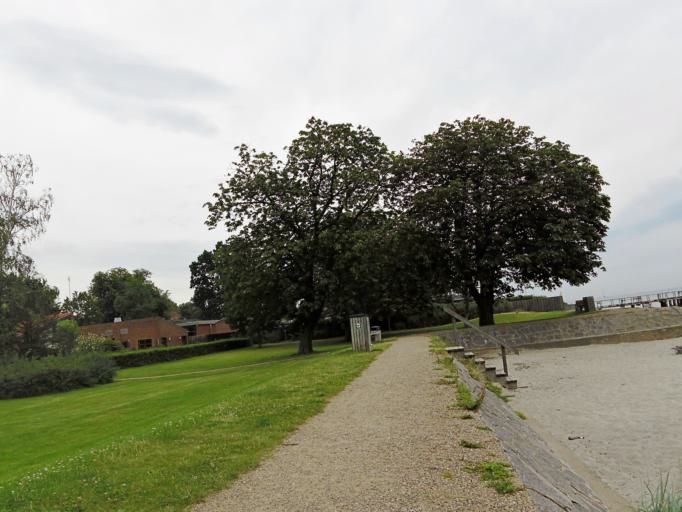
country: DK
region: Capital Region
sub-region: Gentofte Kommune
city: Charlottenlund
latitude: 55.7429
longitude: 12.5870
